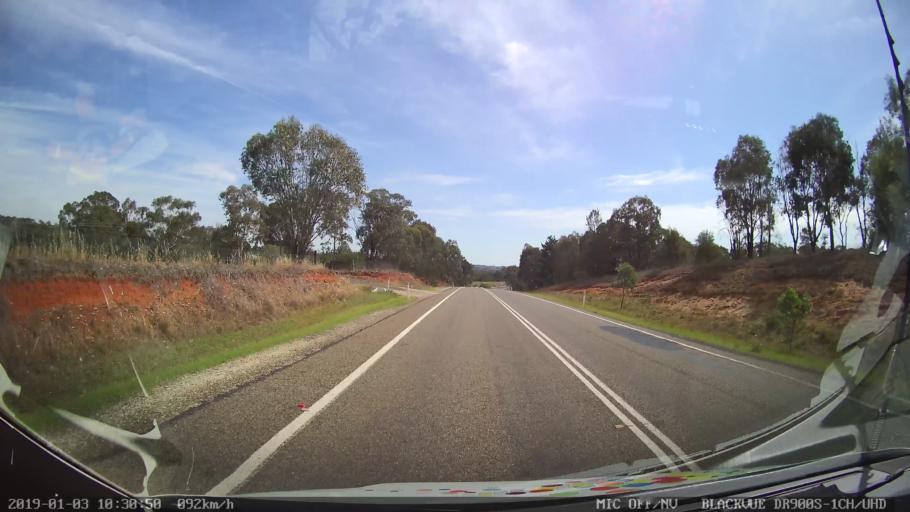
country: AU
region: New South Wales
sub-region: Young
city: Young
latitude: -34.3576
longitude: 148.2720
